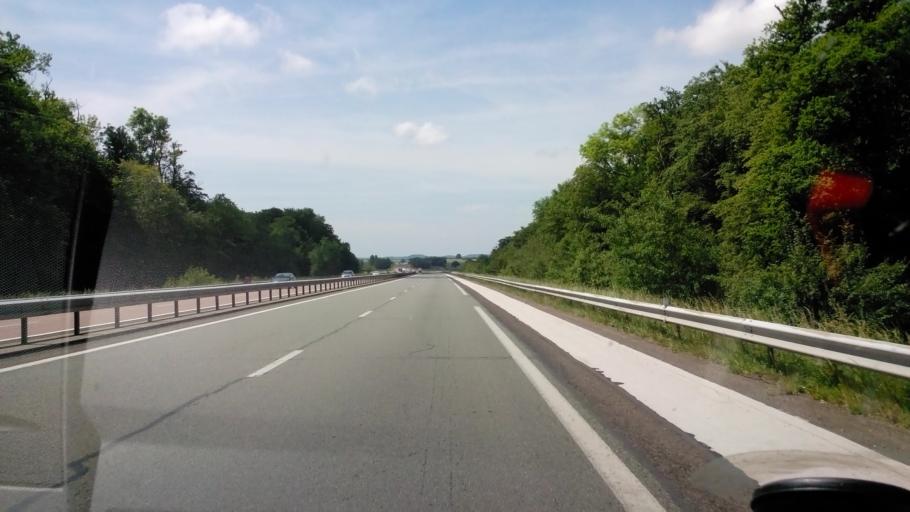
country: FR
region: Champagne-Ardenne
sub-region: Departement de la Haute-Marne
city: Saulxures
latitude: 48.0635
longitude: 5.5875
